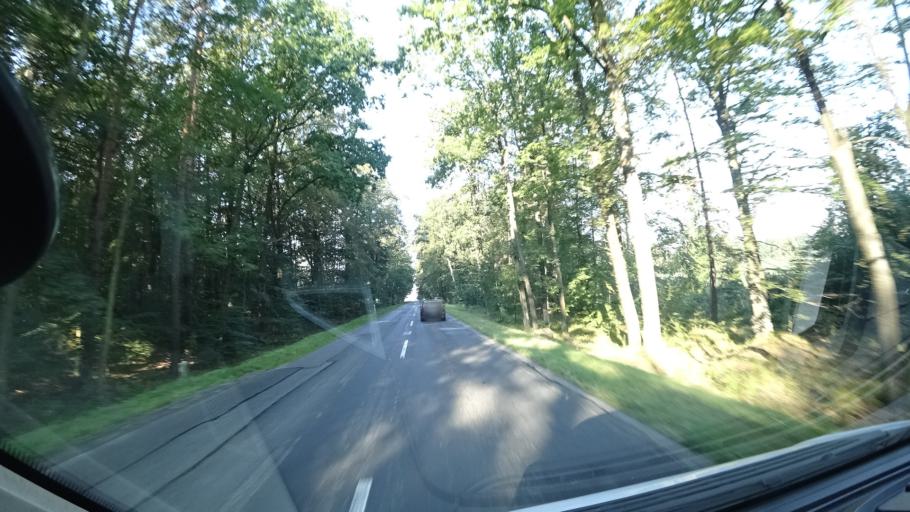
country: PL
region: Silesian Voivodeship
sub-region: Powiat gliwicki
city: Sosnicowice
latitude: 50.2795
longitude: 18.4912
